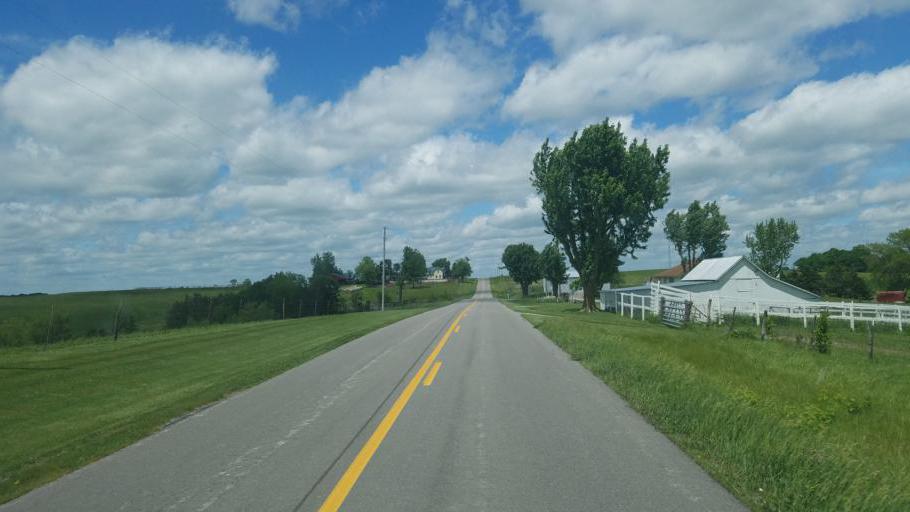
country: US
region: Missouri
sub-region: Harrison County
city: Bethany
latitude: 40.4316
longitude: -94.0640
